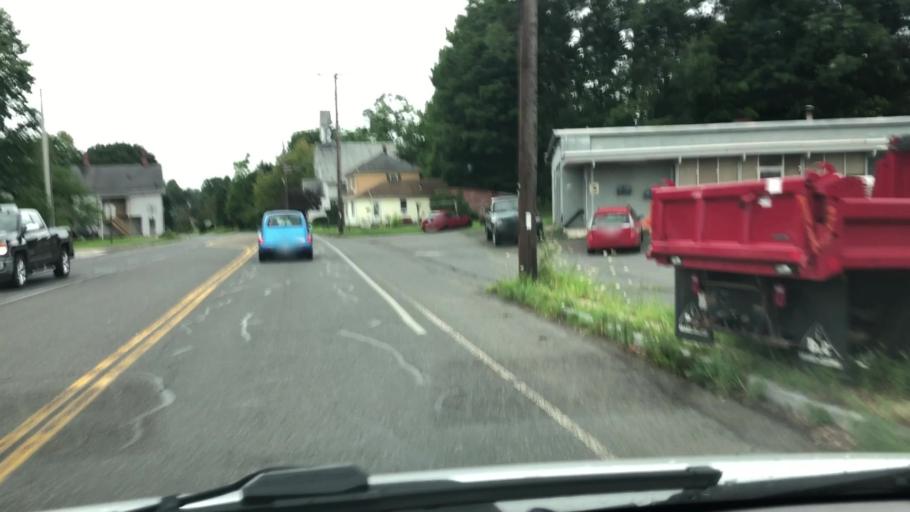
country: US
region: Massachusetts
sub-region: Hampshire County
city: Northampton
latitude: 42.3107
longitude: -72.6478
